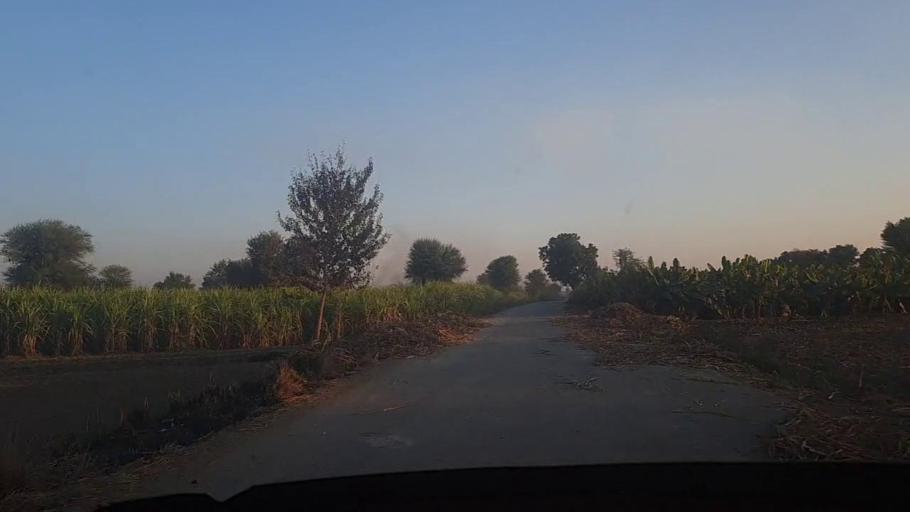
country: PK
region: Sindh
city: Sobhadero
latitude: 27.3476
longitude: 68.3755
